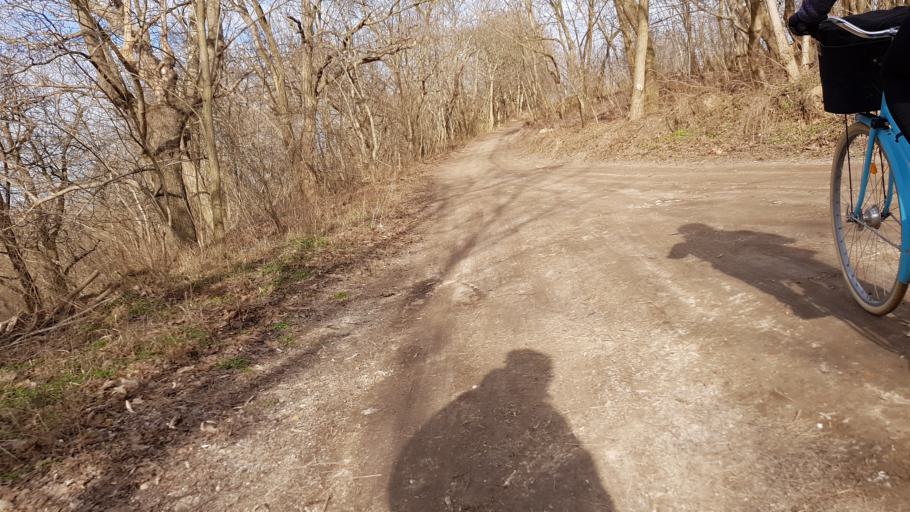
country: PL
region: West Pomeranian Voivodeship
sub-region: Powiat gryfinski
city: Gryfino
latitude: 53.2422
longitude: 14.4928
